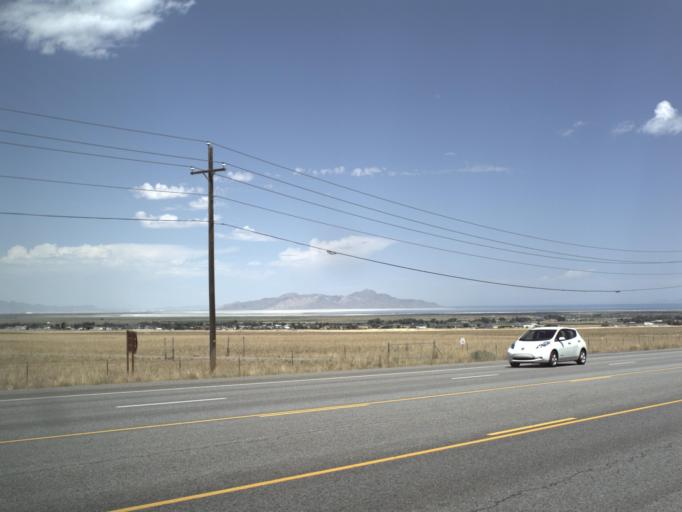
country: US
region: Utah
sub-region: Tooele County
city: Tooele
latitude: 40.5721
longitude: -112.2950
